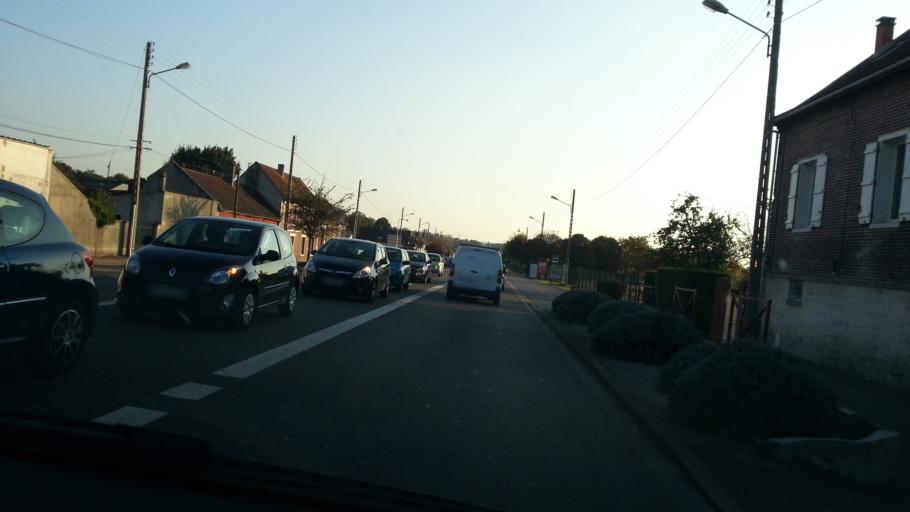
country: FR
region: Picardie
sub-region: Departement de l'Oise
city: Saint-Martin-Longueau
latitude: 49.3422
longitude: 2.6063
